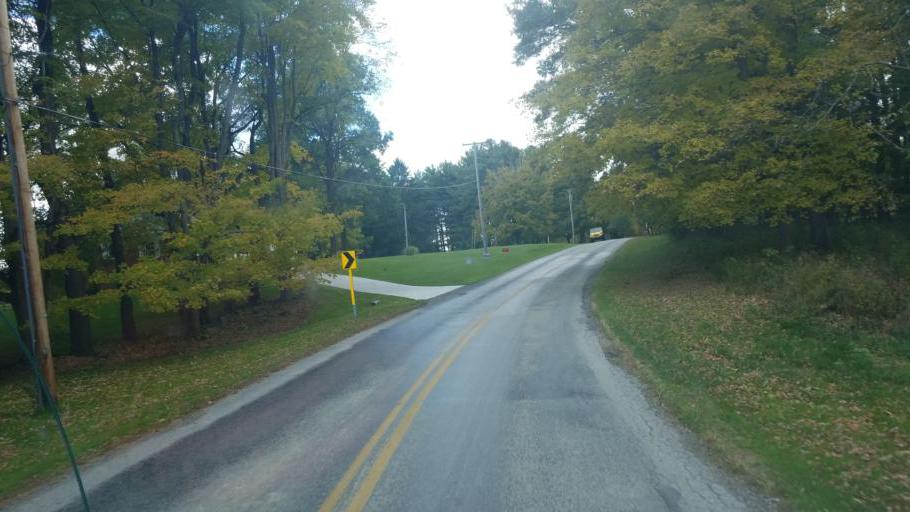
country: US
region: Ohio
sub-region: Richland County
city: Ontario
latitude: 40.7341
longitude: -82.5800
